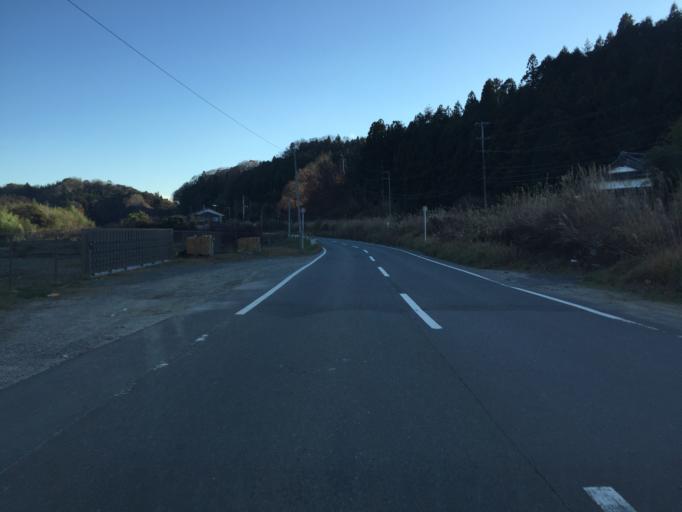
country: JP
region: Fukushima
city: Iwaki
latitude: 37.0962
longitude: 140.8599
